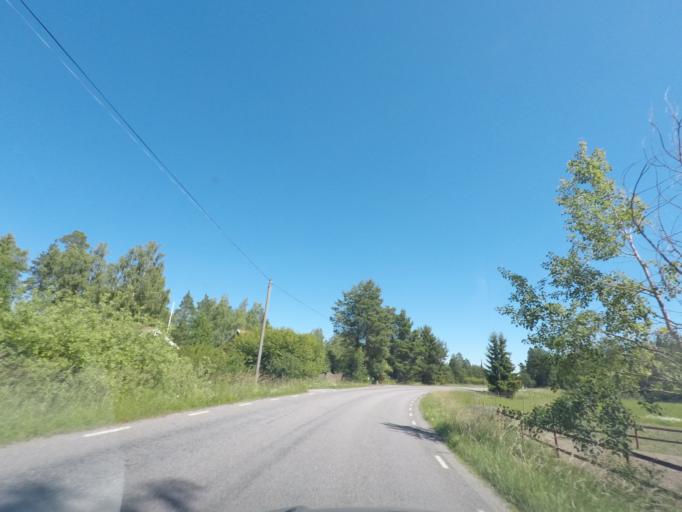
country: SE
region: Uppsala
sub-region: Enkopings Kommun
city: Irsta
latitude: 59.6744
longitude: 16.9040
